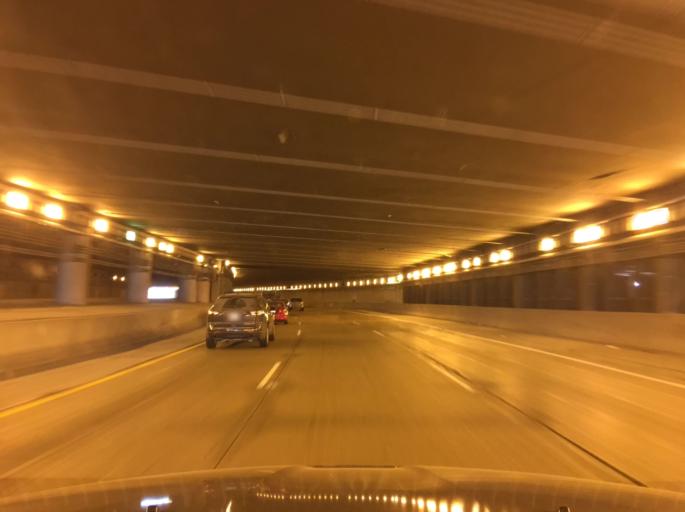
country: US
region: Michigan
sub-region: Wayne County
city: Detroit
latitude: 42.3261
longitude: -83.0507
